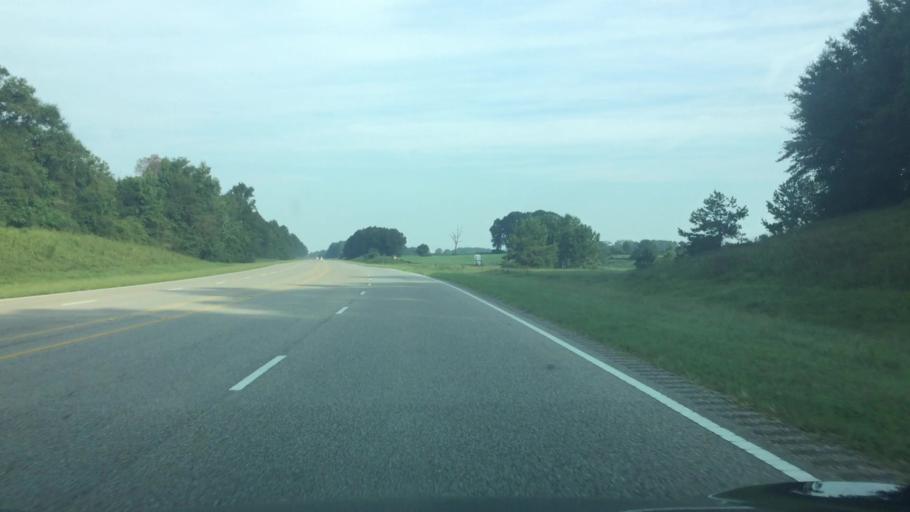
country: US
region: Alabama
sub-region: Covington County
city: Andalusia
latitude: 31.3982
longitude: -86.5780
